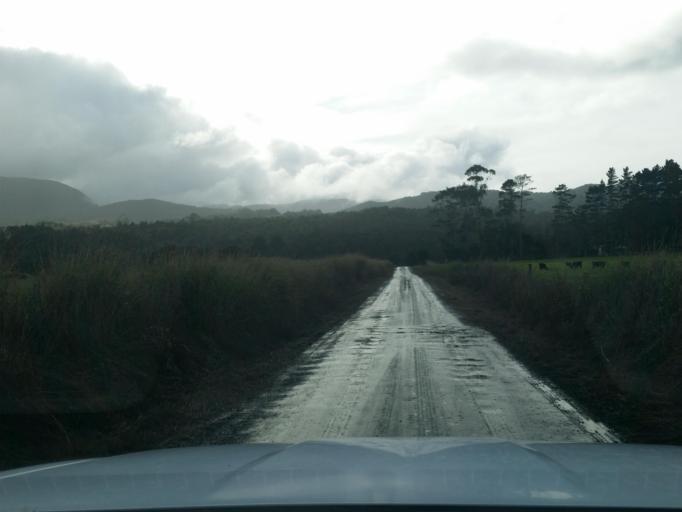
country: NZ
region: Northland
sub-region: Kaipara District
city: Dargaville
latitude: -35.8034
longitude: 173.7406
